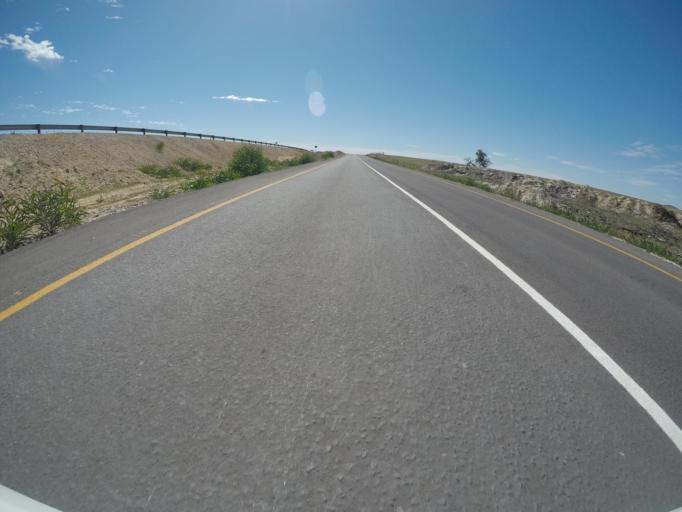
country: ZA
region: Western Cape
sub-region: West Coast District Municipality
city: Malmesbury
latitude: -33.5219
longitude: 18.6510
